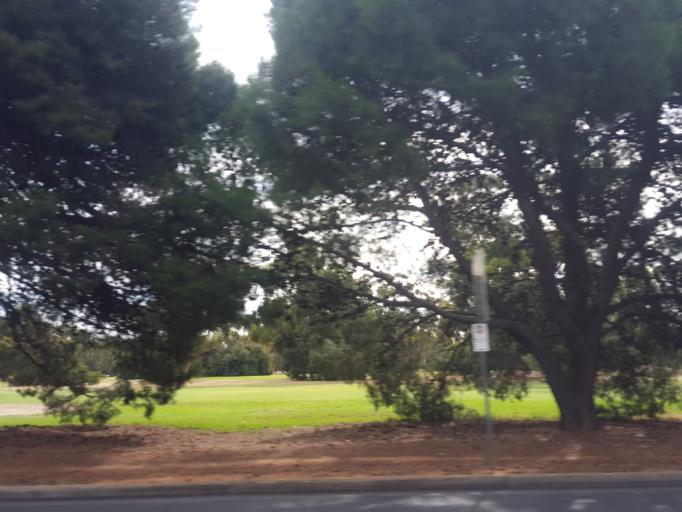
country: AU
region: South Australia
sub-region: Adelaide
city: North Adelaide
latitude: -34.9020
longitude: 138.5896
